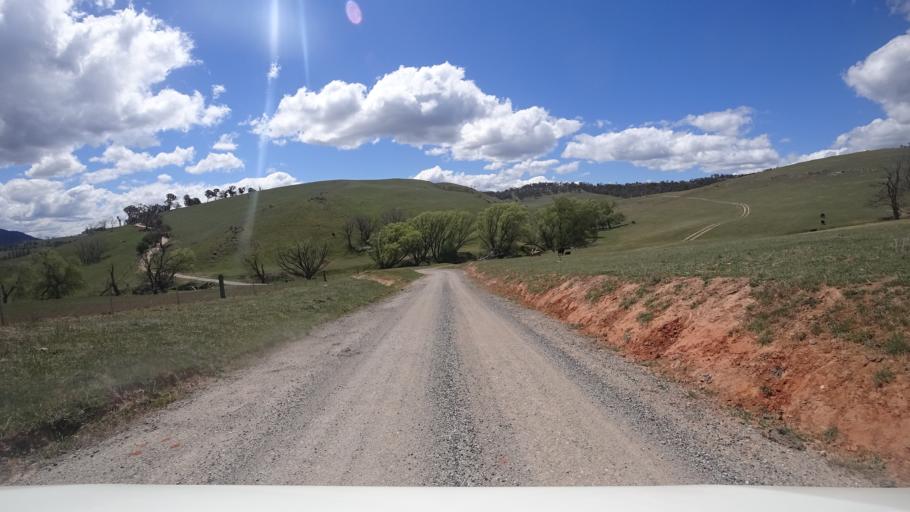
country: AU
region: New South Wales
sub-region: Oberon
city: Oberon
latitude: -33.5768
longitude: 149.9412
